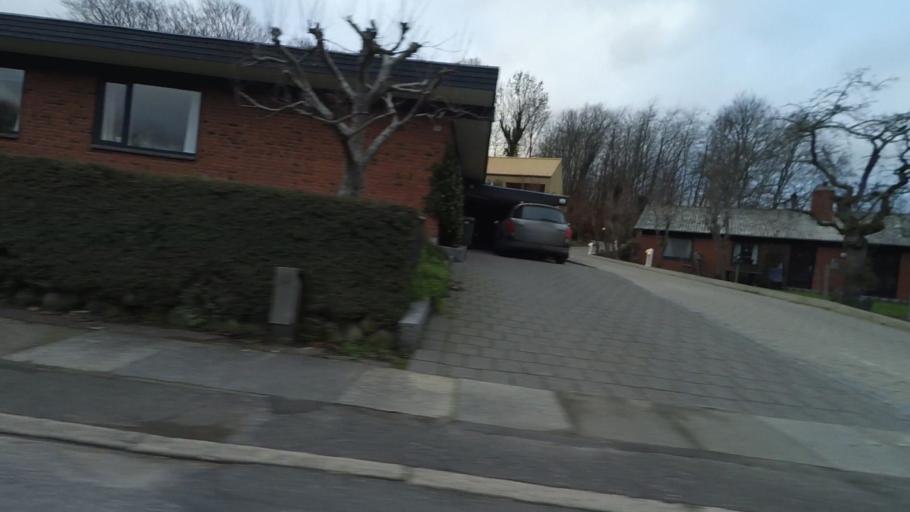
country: DK
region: Central Jutland
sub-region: Arhus Kommune
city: Stavtrup
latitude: 56.1605
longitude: 10.1201
